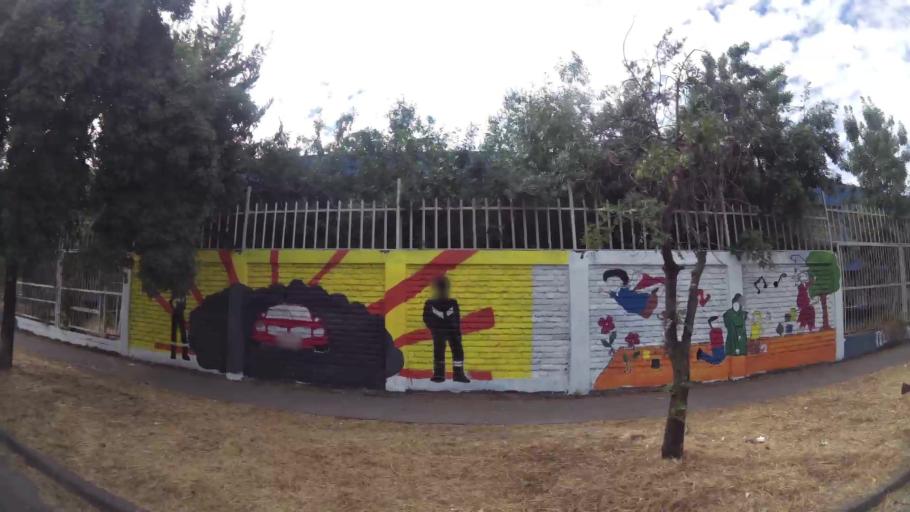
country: CL
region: Santiago Metropolitan
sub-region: Provincia de Santiago
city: La Pintana
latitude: -33.5793
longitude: -70.6417
